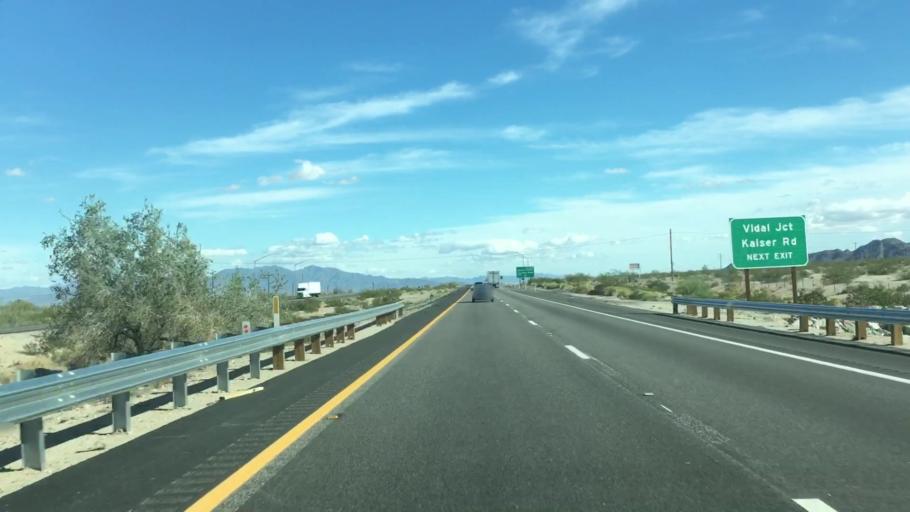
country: US
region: California
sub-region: Imperial County
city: Niland
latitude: 33.7103
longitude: -115.4069
